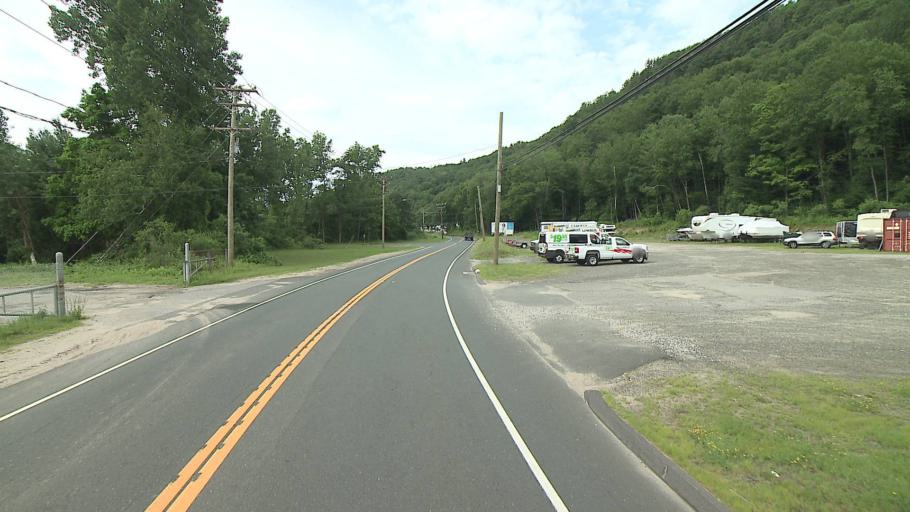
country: US
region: Connecticut
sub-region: Litchfield County
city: Winsted
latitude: 41.9118
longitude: -73.0651
